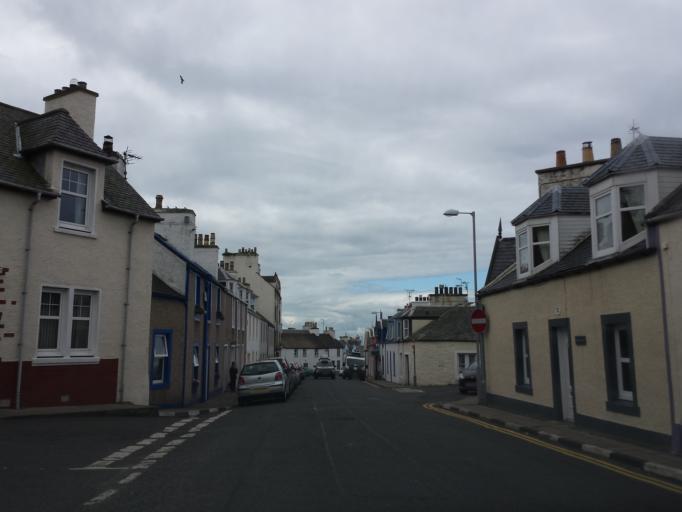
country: GB
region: Scotland
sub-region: Dumfries and Galloway
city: Stranraer
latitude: 54.8430
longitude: -5.1154
